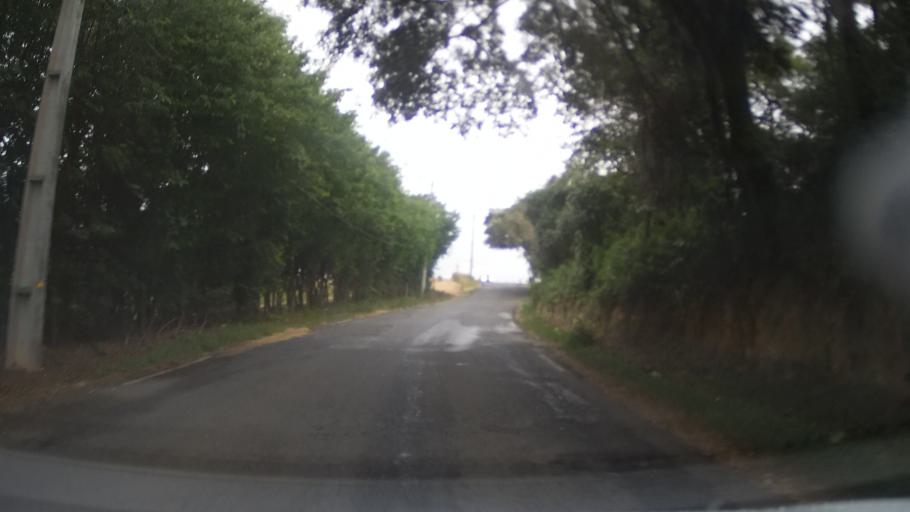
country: BR
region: Sao Paulo
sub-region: Itupeva
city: Itupeva
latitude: -23.1885
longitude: -47.0682
